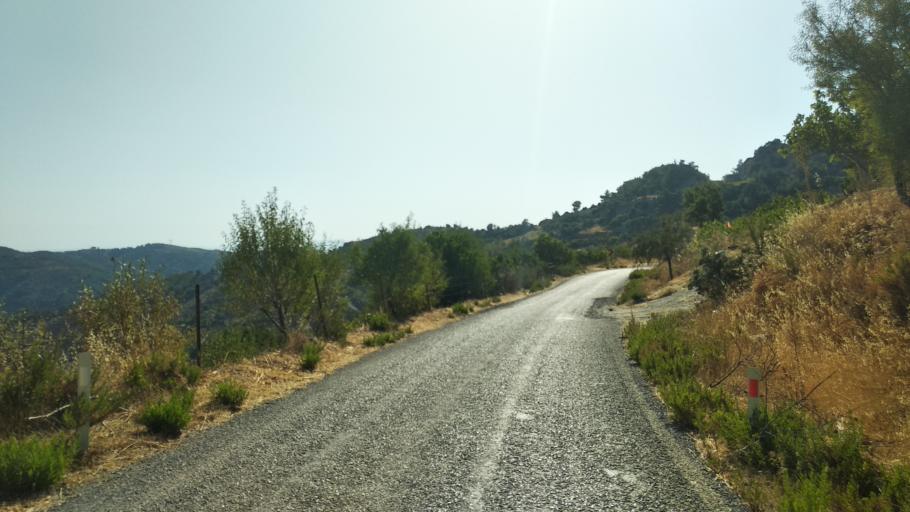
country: TR
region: Izmir
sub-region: Seferihisar
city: Seferhisar
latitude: 38.3217
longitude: 26.9354
